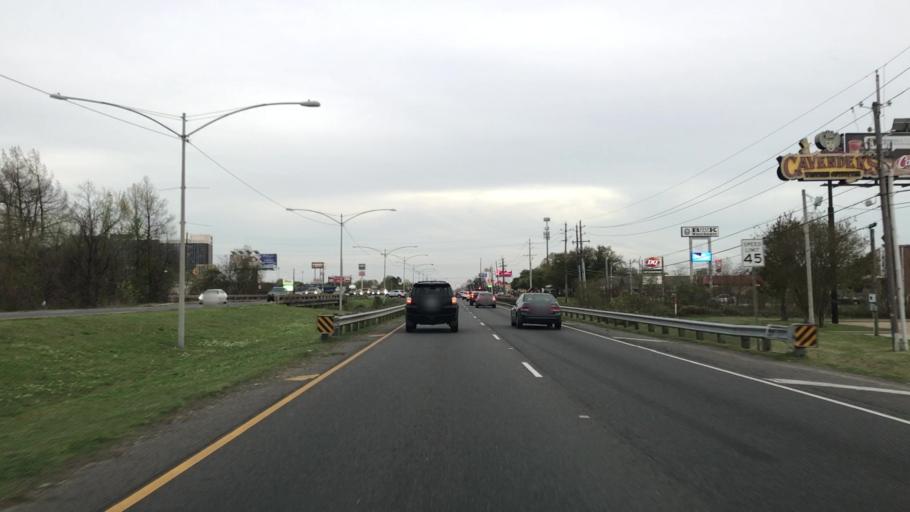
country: US
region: Louisiana
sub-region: Bossier Parish
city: Bossier City
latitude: 32.4358
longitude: -93.7143
